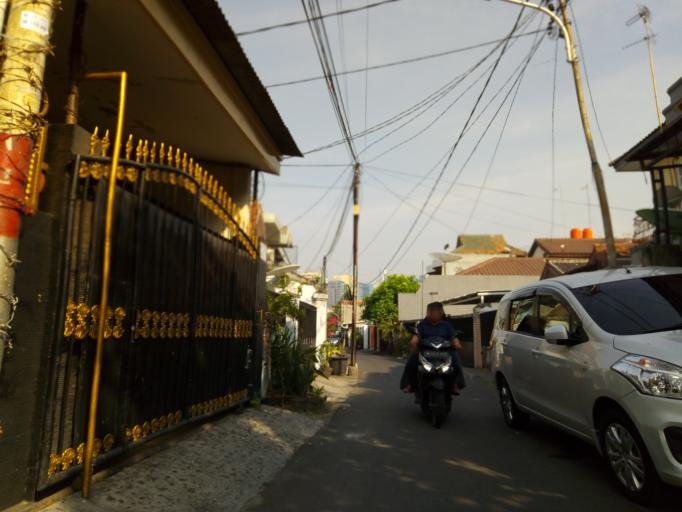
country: ID
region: Jakarta Raya
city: Jakarta
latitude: -6.2131
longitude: 106.8421
